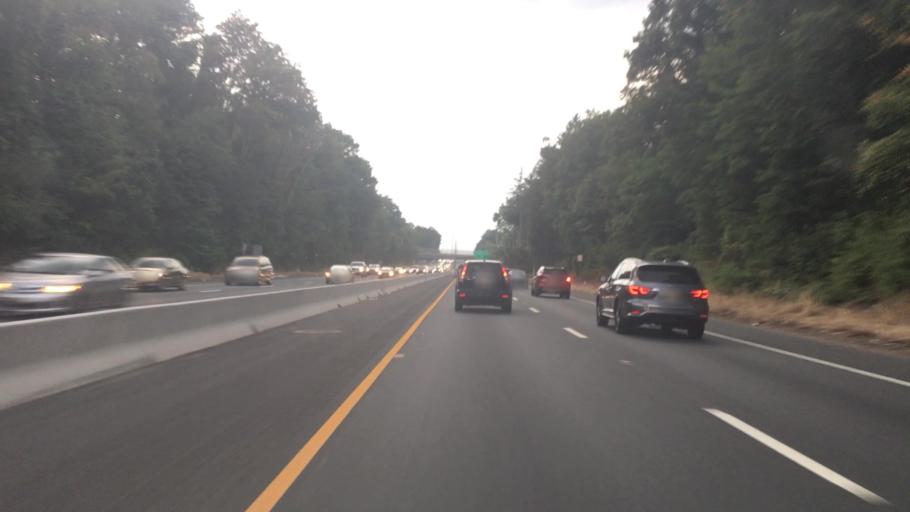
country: US
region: New Jersey
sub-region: Bergen County
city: Franklin Lakes
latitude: 41.0098
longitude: -74.1984
